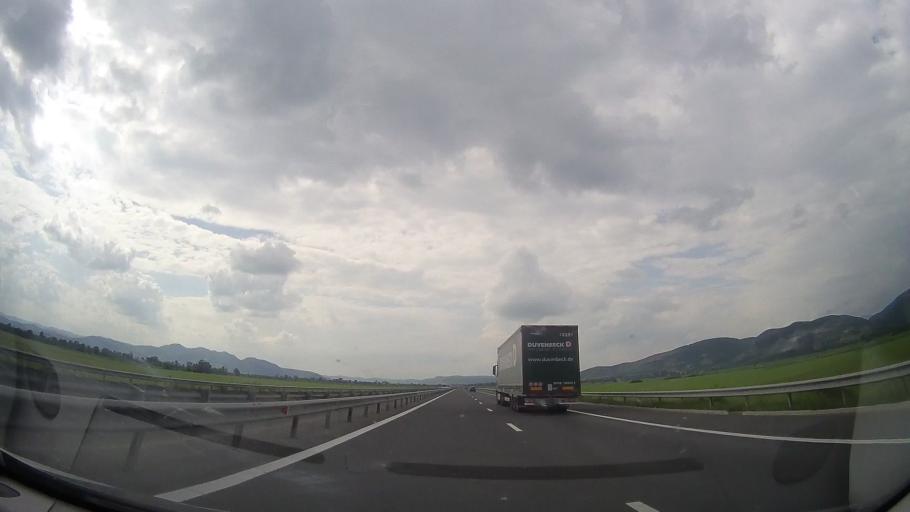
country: RO
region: Hunedoara
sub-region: Oras Simeria
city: Simeria
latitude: 45.8731
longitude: 23.0109
